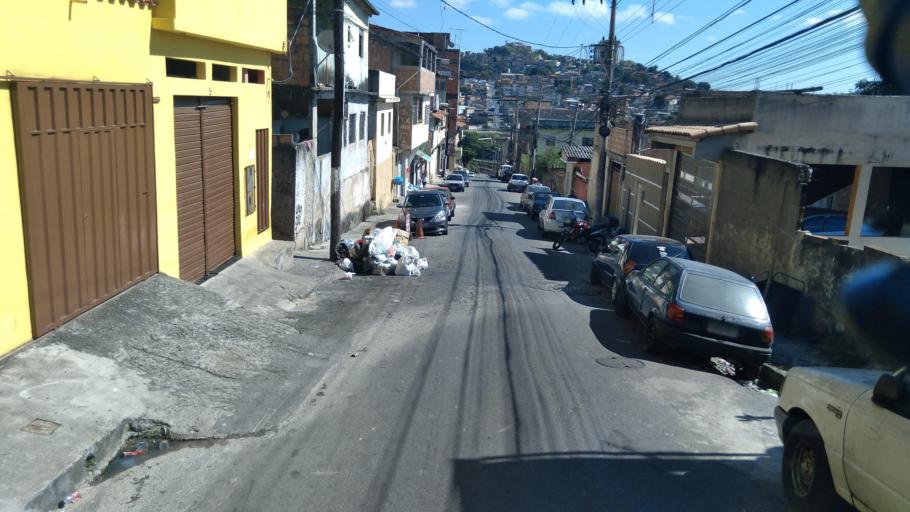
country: BR
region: Minas Gerais
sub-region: Belo Horizonte
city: Belo Horizonte
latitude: -19.9070
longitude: -43.8890
